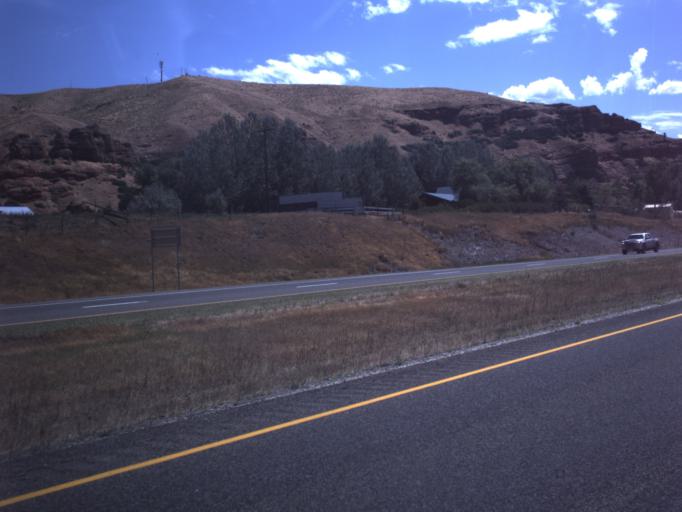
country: US
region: Utah
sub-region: Summit County
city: Coalville
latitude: 40.9811
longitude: -111.4479
